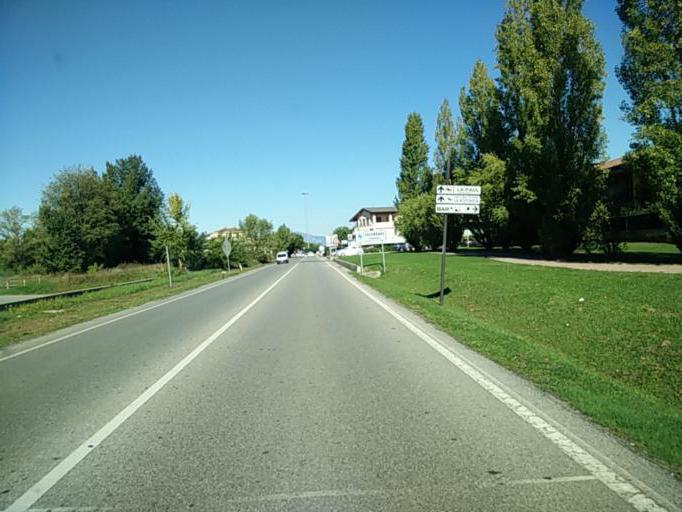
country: IT
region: Lombardy
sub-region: Provincia di Brescia
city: San Martino della Battaglia
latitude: 45.4625
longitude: 10.6011
